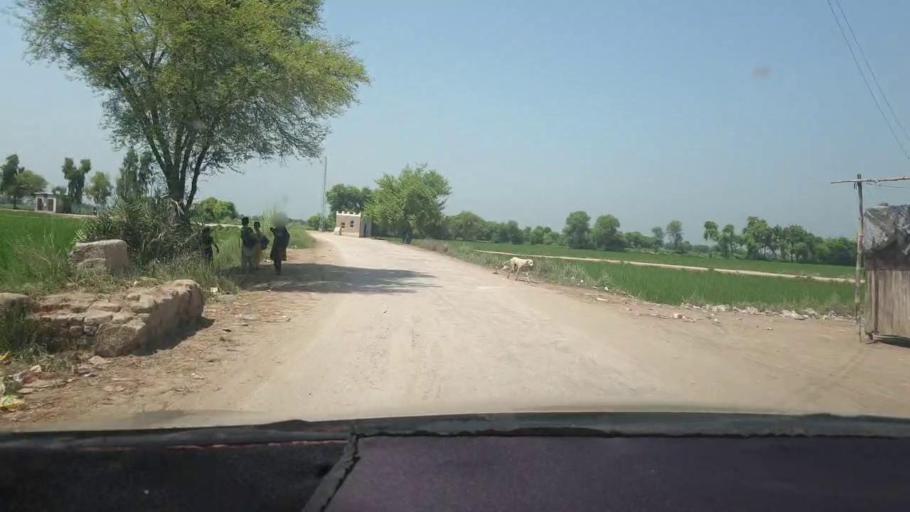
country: PK
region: Sindh
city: Miro Khan
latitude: 27.6712
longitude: 68.0600
